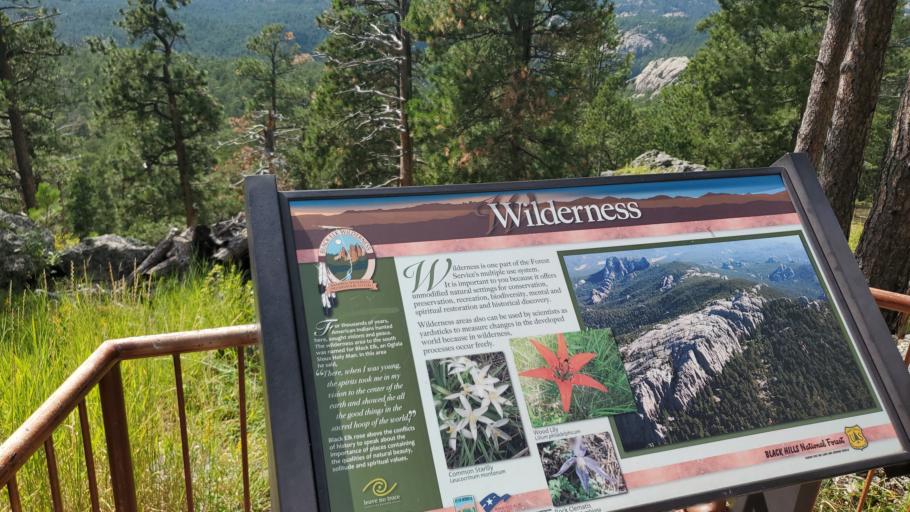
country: US
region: South Dakota
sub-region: Custer County
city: Custer
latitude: 43.8577
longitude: -103.4346
